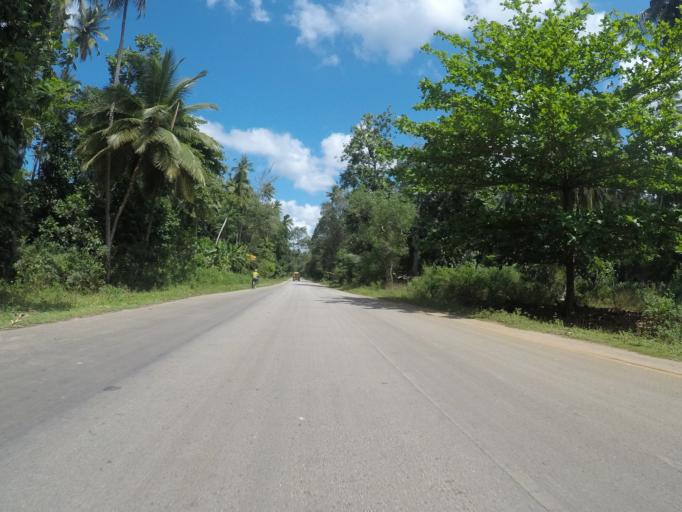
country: TZ
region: Zanzibar Central/South
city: Koani
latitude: -6.1441
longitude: 39.3276
